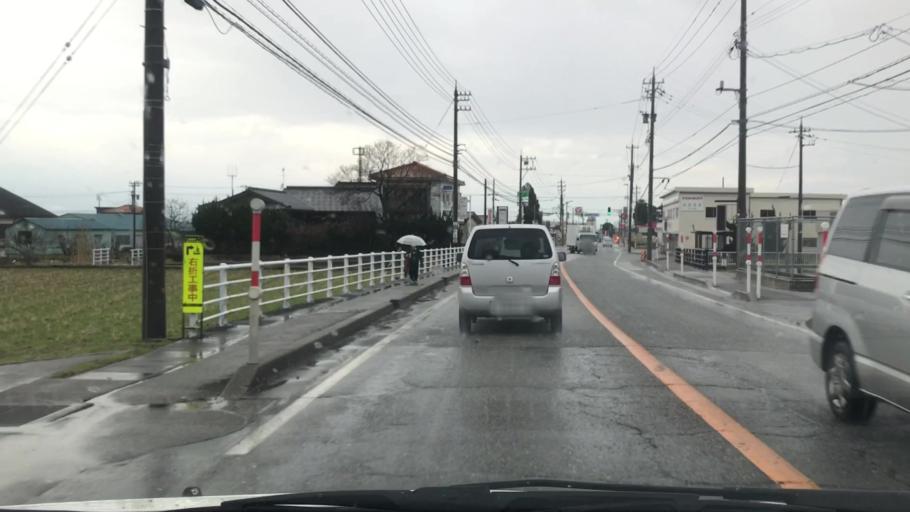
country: JP
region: Toyama
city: Yatsuomachi-higashikumisaka
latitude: 36.6035
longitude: 137.2033
